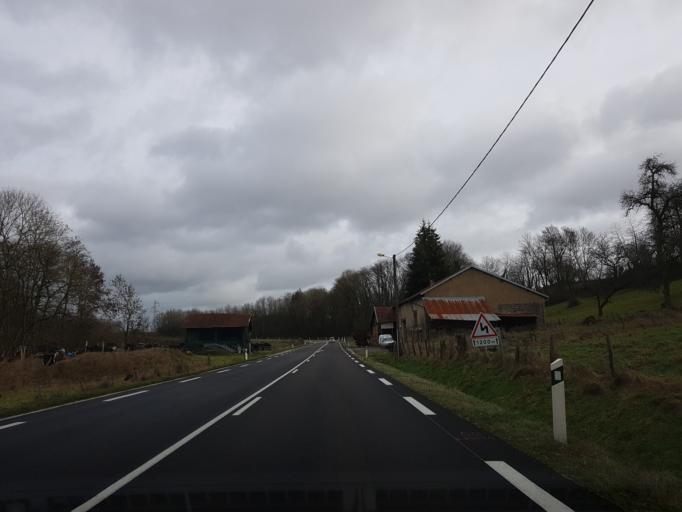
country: FR
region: Champagne-Ardenne
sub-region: Departement de la Haute-Marne
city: Langres
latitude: 47.8567
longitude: 5.3793
